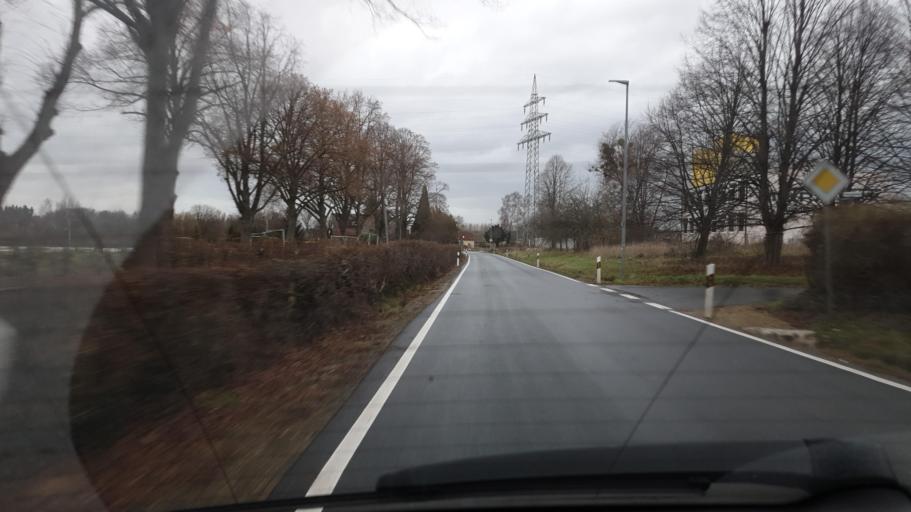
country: DE
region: North Rhine-Westphalia
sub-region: Regierungsbezirk Detmold
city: Lage
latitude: 51.9843
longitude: 8.8442
